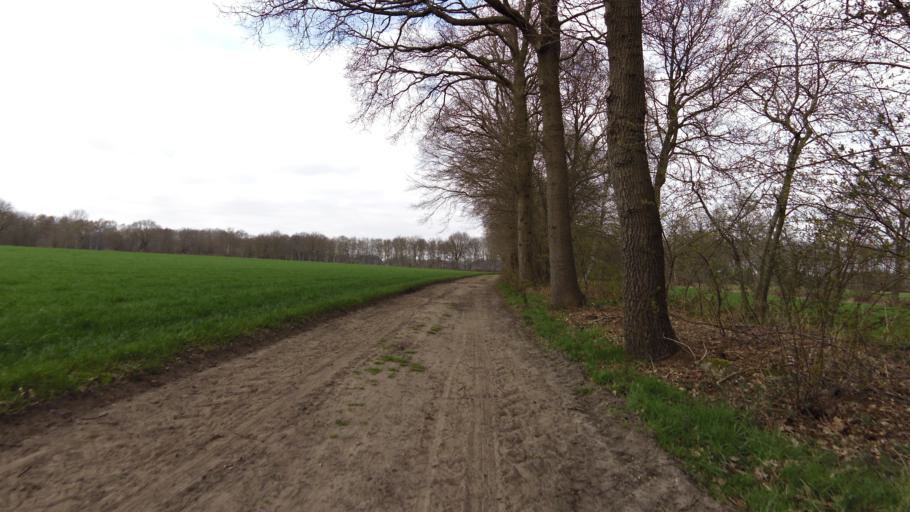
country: NL
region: Gelderland
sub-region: Gemeente Nijkerk
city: Nijkerk
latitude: 52.2261
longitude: 5.5492
